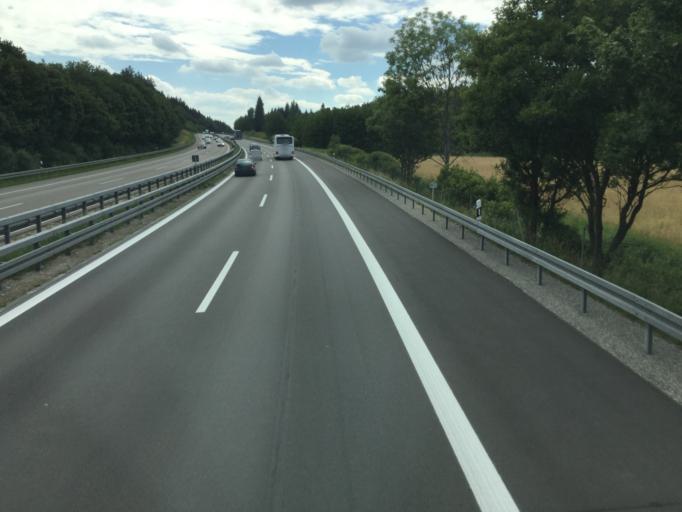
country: DE
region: Bavaria
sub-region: Swabia
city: Waal
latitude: 48.0459
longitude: 10.8113
